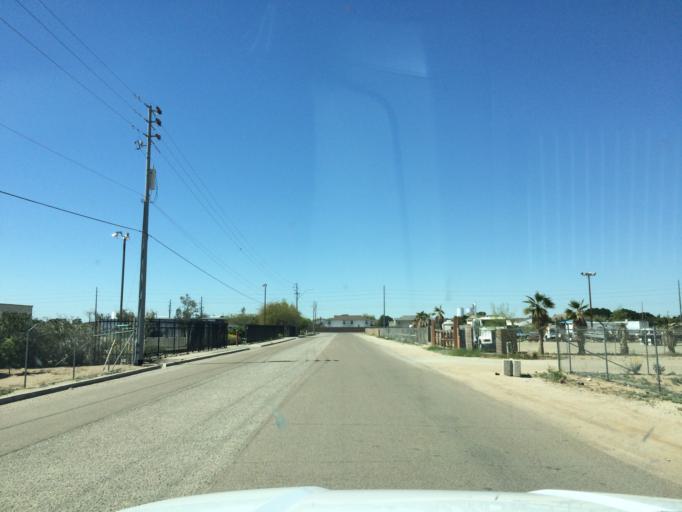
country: US
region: Arizona
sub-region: Yuma County
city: Yuma
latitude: 32.6515
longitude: -114.5787
